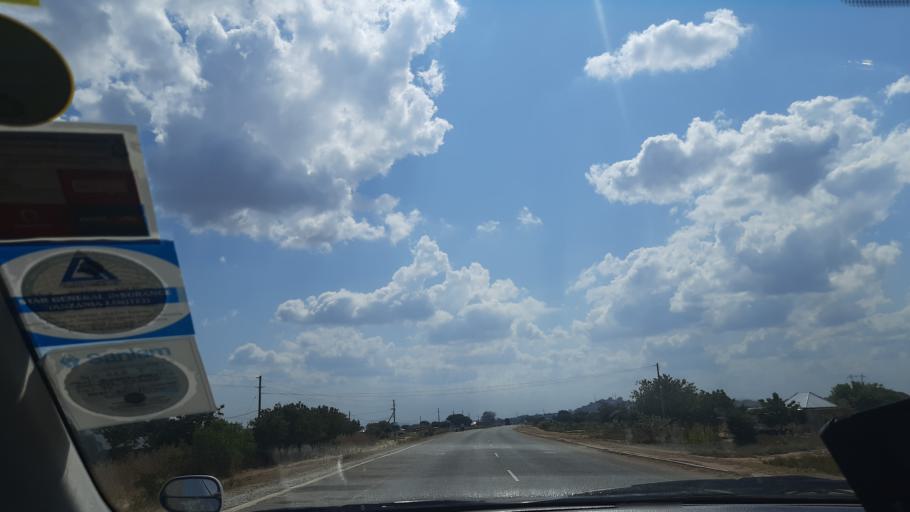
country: TZ
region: Singida
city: Kintinku
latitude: -5.9636
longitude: 35.3277
